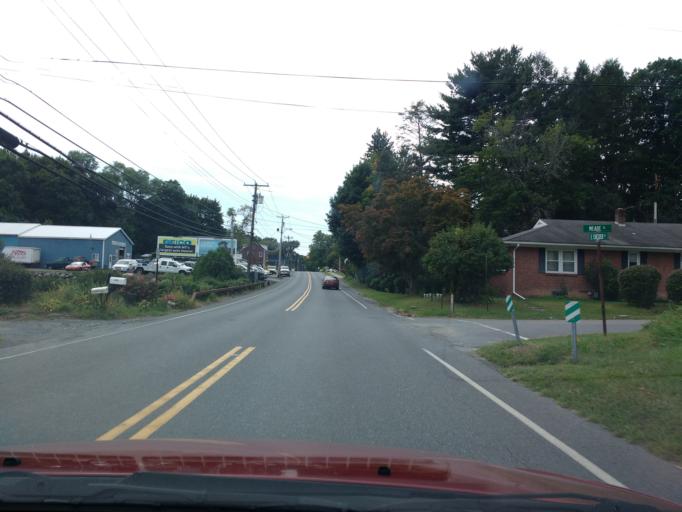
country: US
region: New York
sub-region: Ulster County
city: Lincoln Park
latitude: 41.9388
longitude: -73.9854
